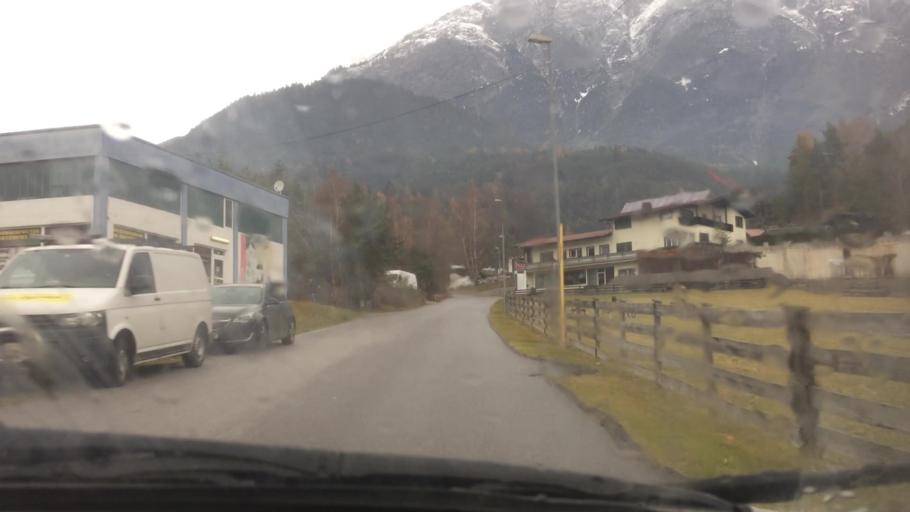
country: AT
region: Tyrol
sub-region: Politischer Bezirk Innsbruck Land
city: Pfaffenhofen
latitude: 47.3162
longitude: 11.0974
